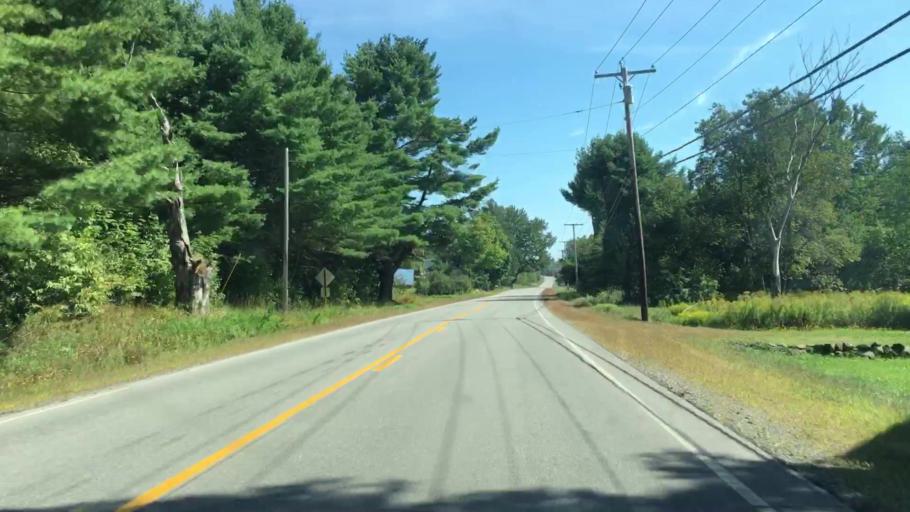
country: US
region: Maine
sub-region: Piscataquis County
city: Milo
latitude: 45.1877
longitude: -68.8934
